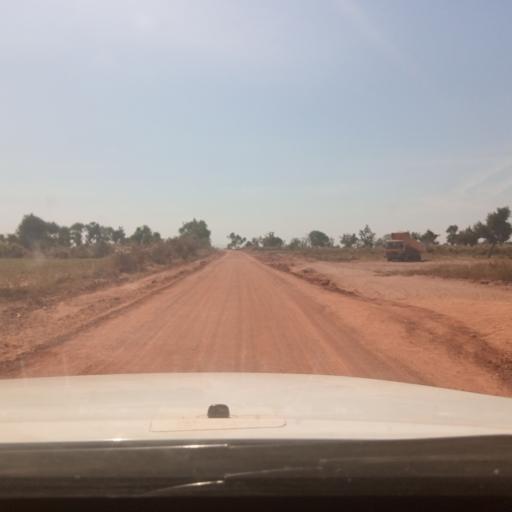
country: NG
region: Adamawa
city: Yola
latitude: 9.1833
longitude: 12.7499
